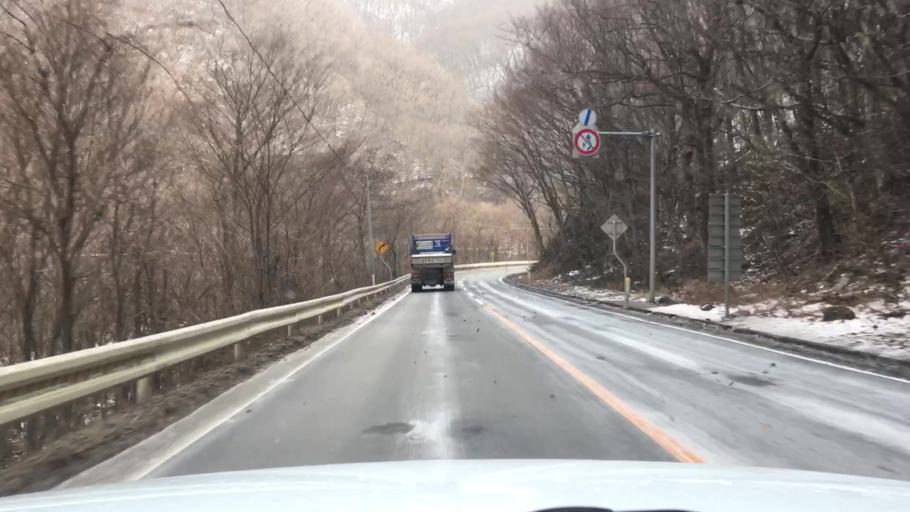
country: JP
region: Iwate
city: Tono
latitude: 39.6197
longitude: 141.5044
